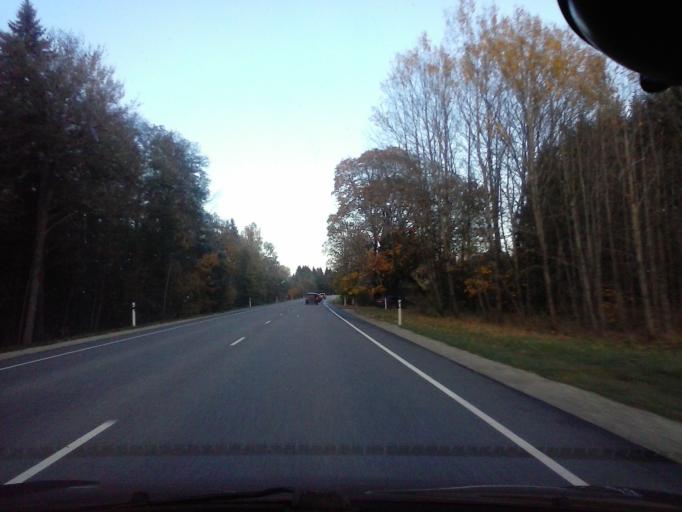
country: EE
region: Harju
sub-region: Nissi vald
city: Turba
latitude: 58.9897
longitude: 24.0202
